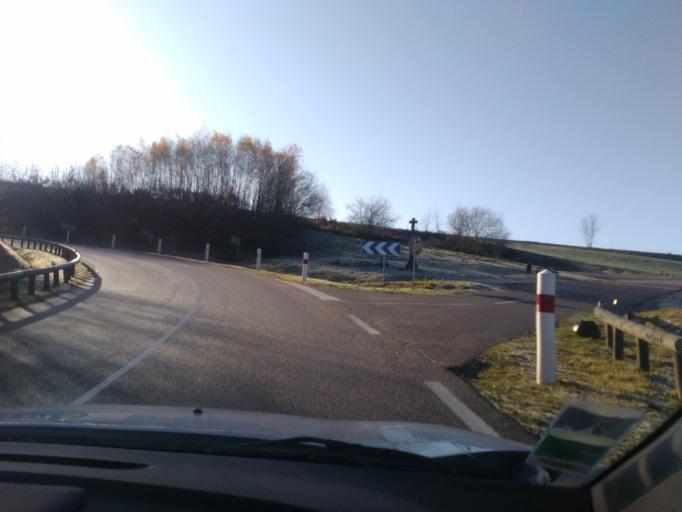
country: FR
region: Lorraine
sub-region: Departement des Vosges
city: Xertigny
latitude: 48.0357
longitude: 6.4152
